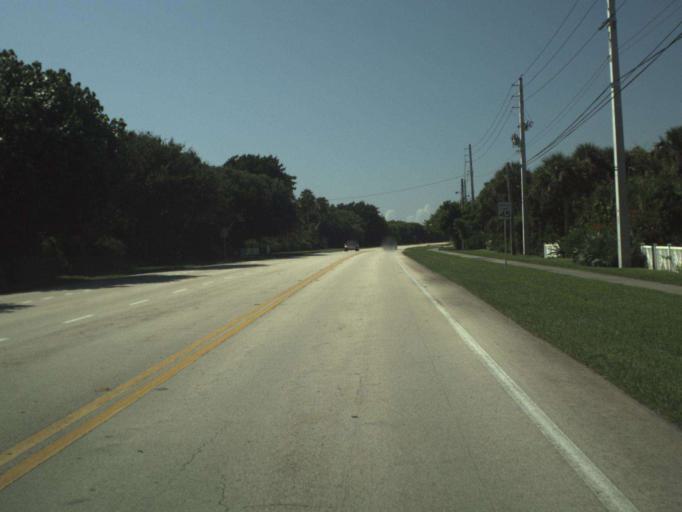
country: US
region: Florida
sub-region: Indian River County
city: Wabasso Beach
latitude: 27.7542
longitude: -80.3928
